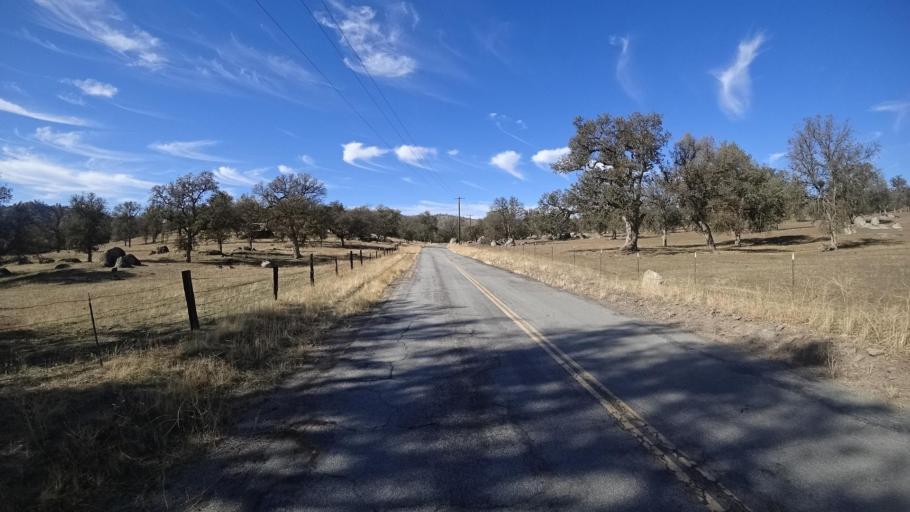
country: US
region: California
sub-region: Kern County
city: Alta Sierra
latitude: 35.6210
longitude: -118.7377
